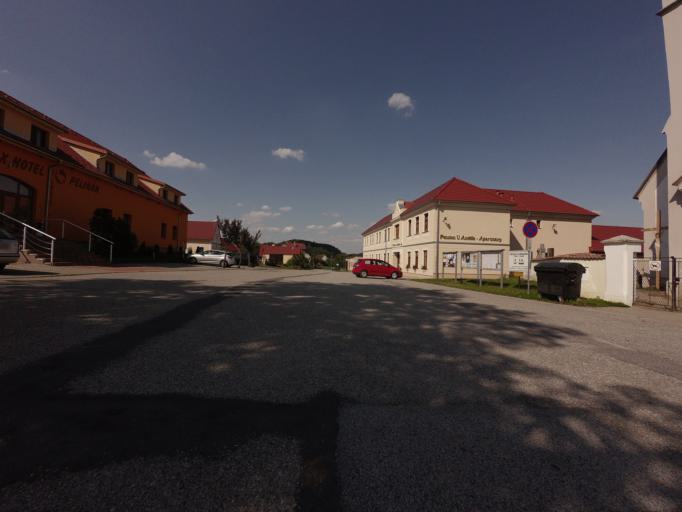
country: CZ
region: Jihocesky
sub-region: Okres Ceske Budejovice
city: Hluboka nad Vltavou
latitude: 49.1291
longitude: 14.4521
